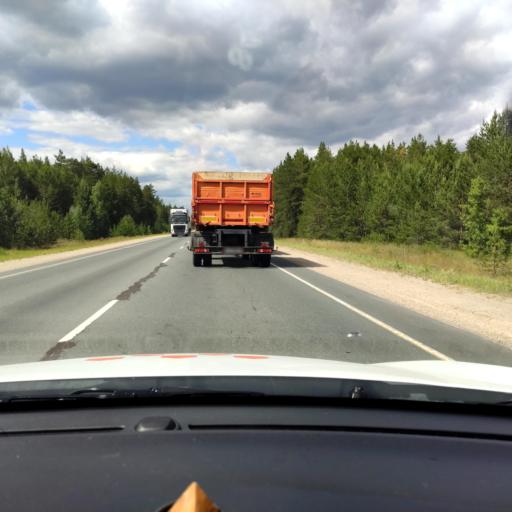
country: RU
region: Mariy-El
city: Krasnogorskiy
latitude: 56.0864
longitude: 48.3521
